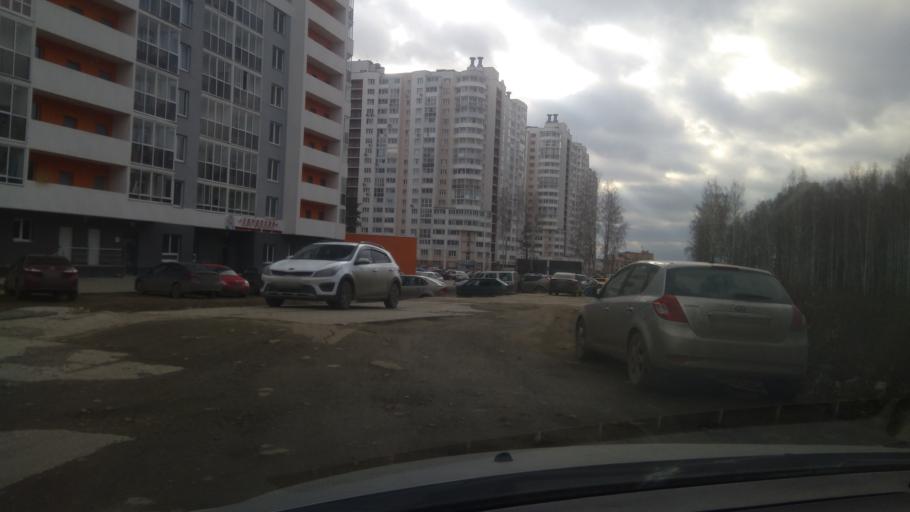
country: RU
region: Sverdlovsk
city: Sovkhoznyy
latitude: 56.7862
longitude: 60.5449
